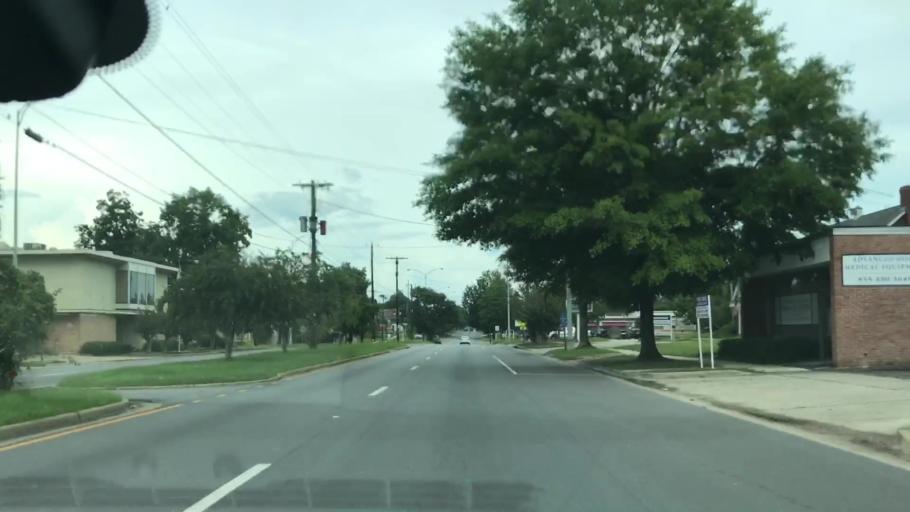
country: US
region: Alabama
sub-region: Barbour County
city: Eufaula
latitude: 31.8914
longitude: -85.1432
